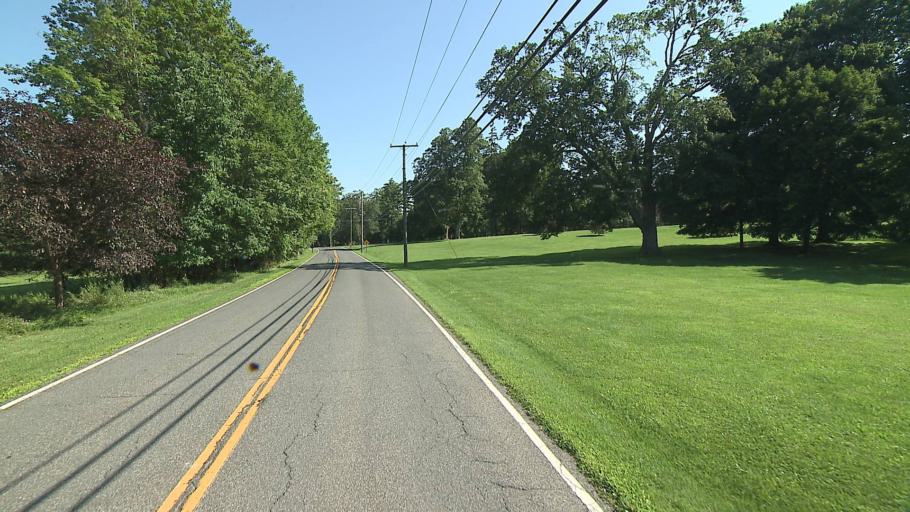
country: US
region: Connecticut
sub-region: Litchfield County
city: Kent
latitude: 41.8664
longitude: -73.4770
